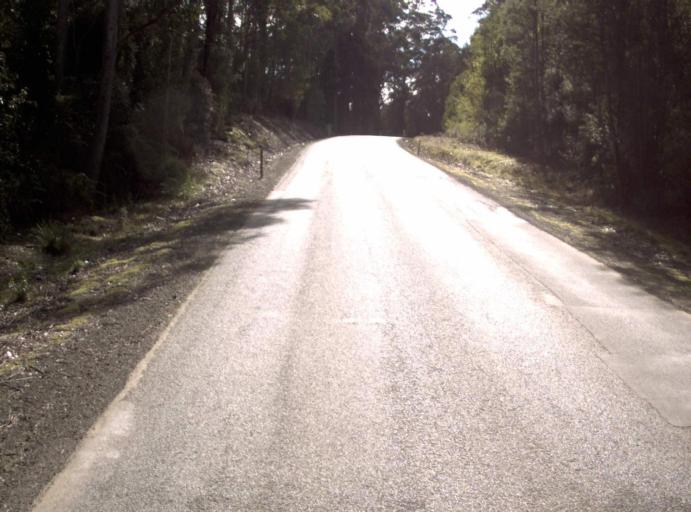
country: AU
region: Tasmania
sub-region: Launceston
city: Mayfield
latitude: -41.2134
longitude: 147.2121
